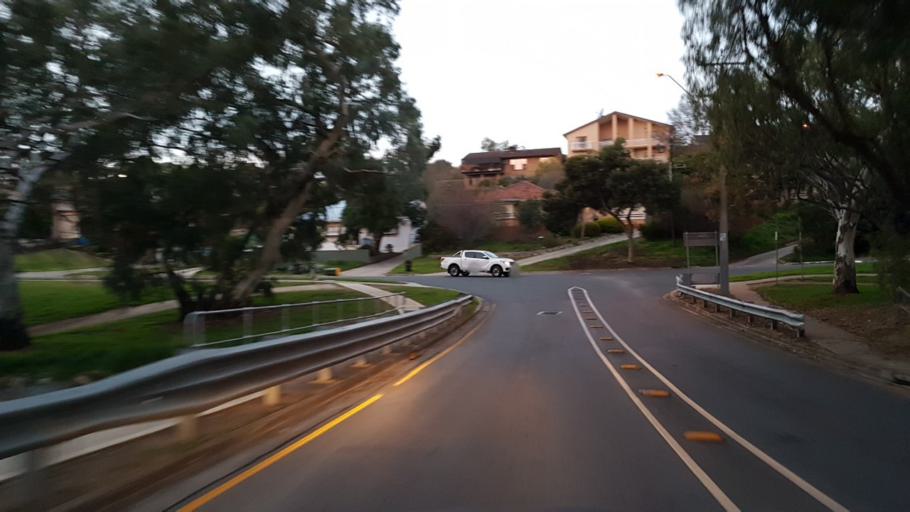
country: AU
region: South Australia
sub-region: Port Adelaide Enfield
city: Gilles Plains
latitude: -34.8389
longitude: 138.6537
